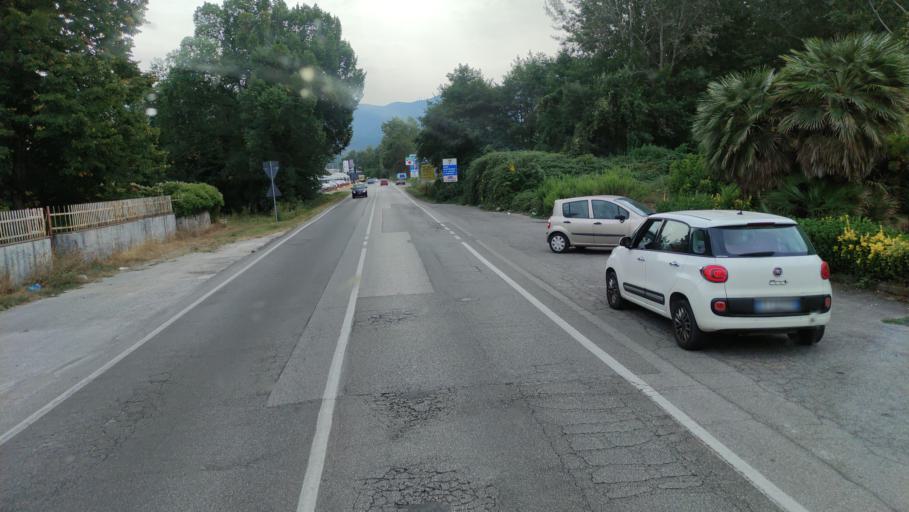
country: IT
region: Tuscany
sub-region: Provincia di Lucca
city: Lucca
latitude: 43.8188
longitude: 10.4923
